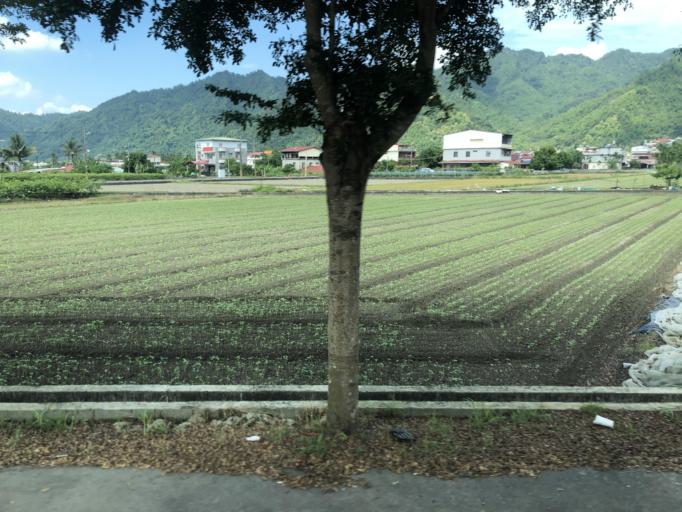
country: TW
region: Taiwan
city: Yujing
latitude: 22.9117
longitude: 120.5629
